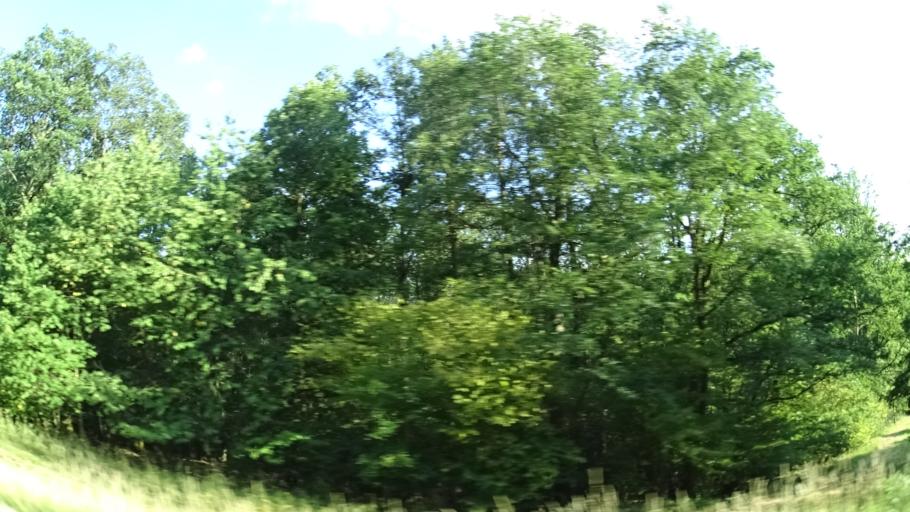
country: DE
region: Bavaria
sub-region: Regierungsbezirk Unterfranken
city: Oberelsbach
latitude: 50.4243
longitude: 10.1483
